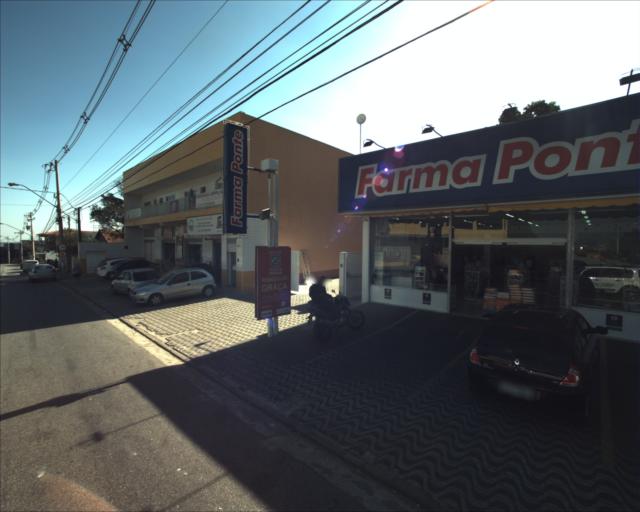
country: BR
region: Sao Paulo
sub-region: Sorocaba
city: Sorocaba
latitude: -23.3994
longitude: -47.3786
